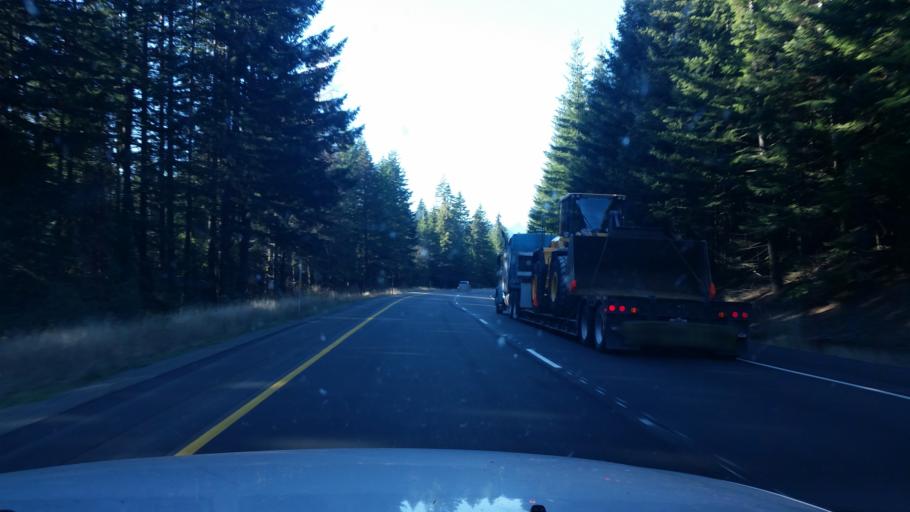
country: US
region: Washington
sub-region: Kittitas County
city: Cle Elum
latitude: 47.3014
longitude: -121.2982
